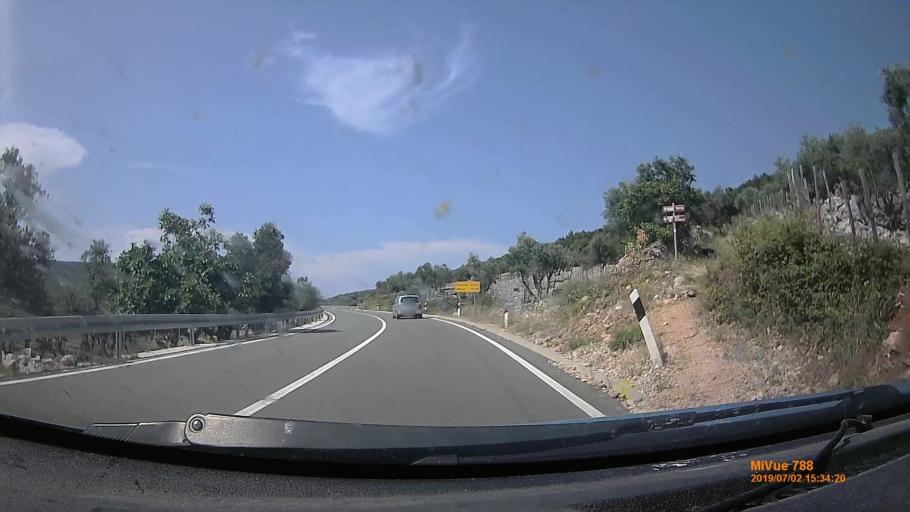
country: HR
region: Primorsko-Goranska
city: Cres
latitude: 44.9661
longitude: 14.4127
